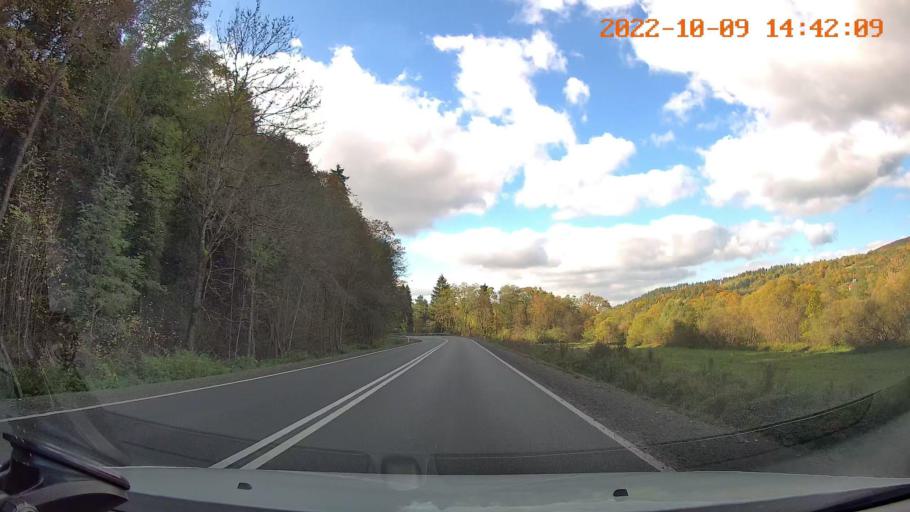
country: PL
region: Lesser Poland Voivodeship
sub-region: Powiat myslenicki
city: Lubien
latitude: 49.7122
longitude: 20.0022
